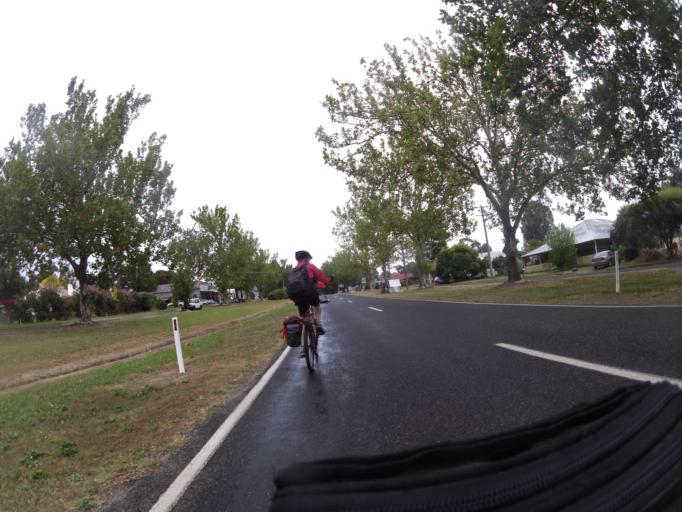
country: AU
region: New South Wales
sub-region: Greater Hume Shire
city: Holbrook
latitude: -36.1909
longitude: 147.7711
